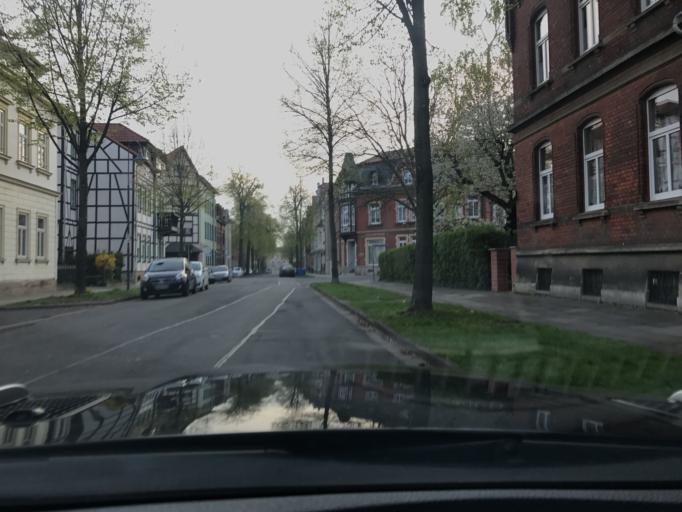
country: DE
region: Thuringia
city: Muehlhausen
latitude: 51.2075
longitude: 10.4694
